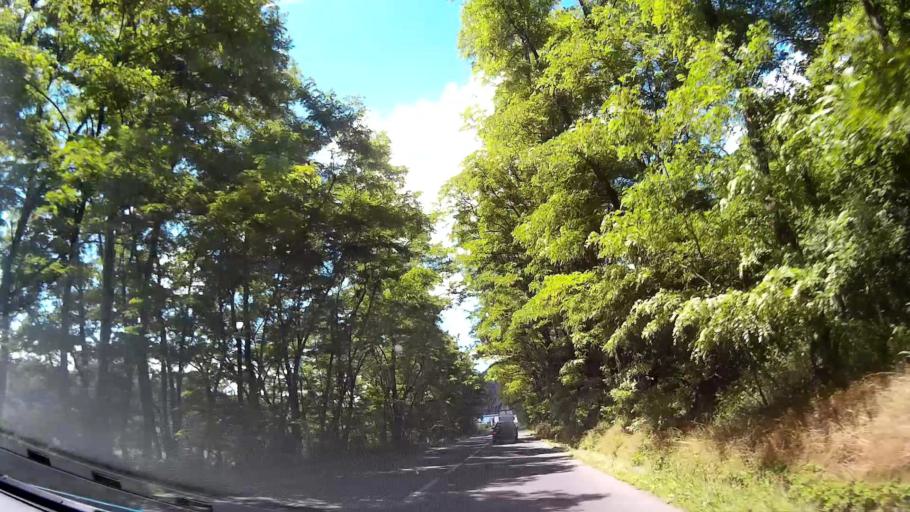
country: CZ
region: South Moravian
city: Oslavany
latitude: 49.1157
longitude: 16.3512
